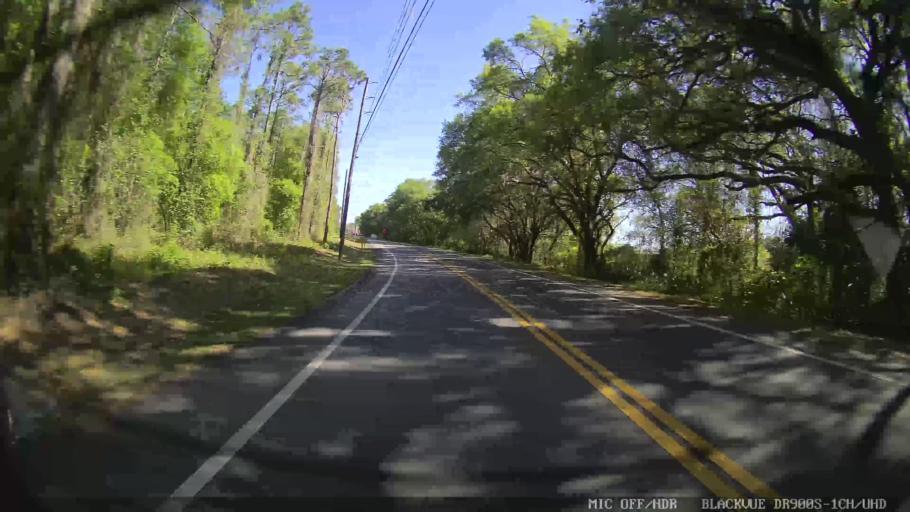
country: US
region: Florida
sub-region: Pasco County
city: Shady Hills
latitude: 28.3344
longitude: -82.5448
